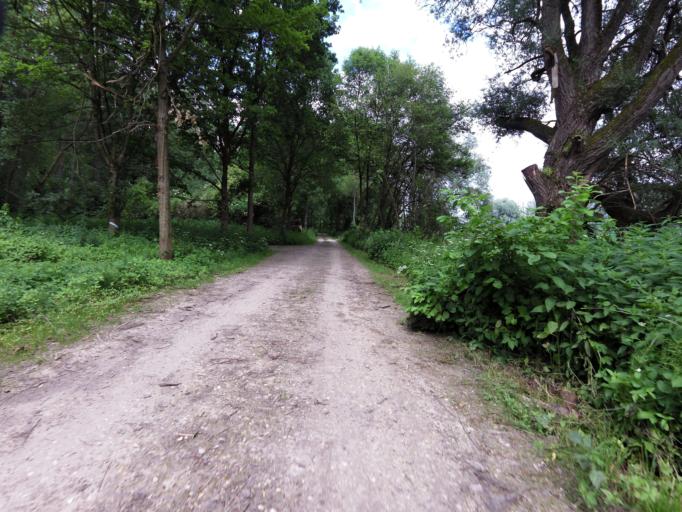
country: DE
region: Bavaria
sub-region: Upper Bavaria
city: Moosburg
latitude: 48.4543
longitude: 11.9453
